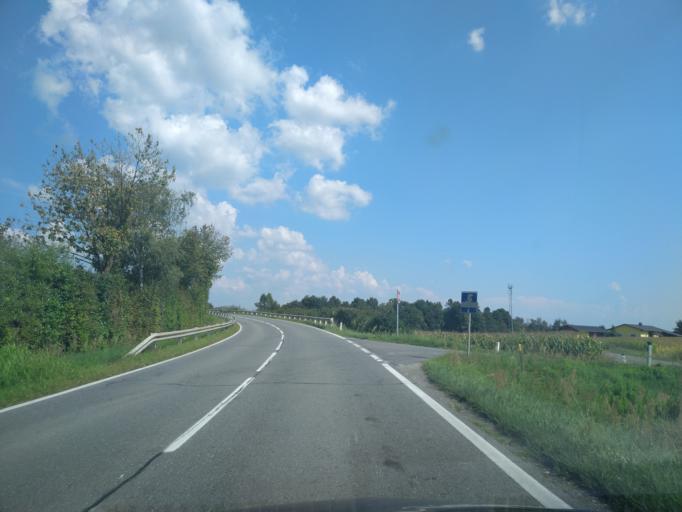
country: AT
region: Styria
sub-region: Politischer Bezirk Leibnitz
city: Obervogau
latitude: 46.7611
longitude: 15.5882
